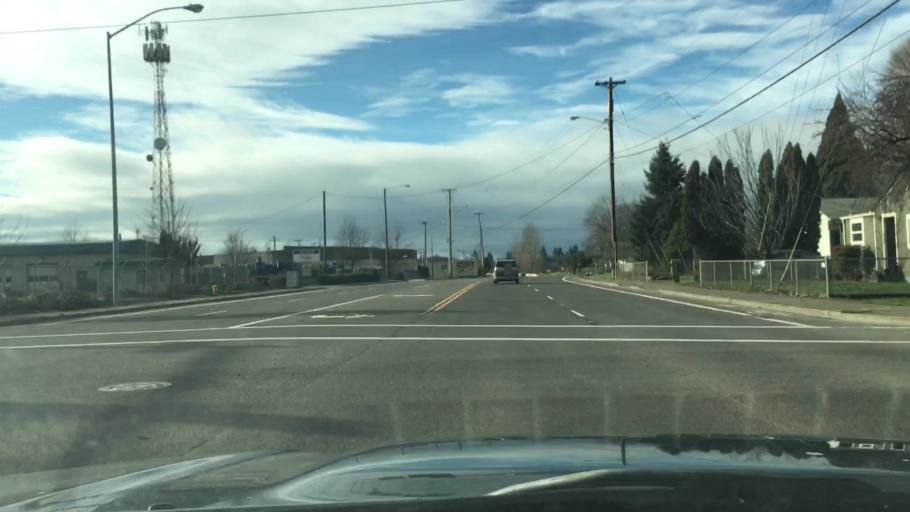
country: US
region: Oregon
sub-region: Lane County
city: Eugene
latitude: 44.0638
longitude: -123.1402
